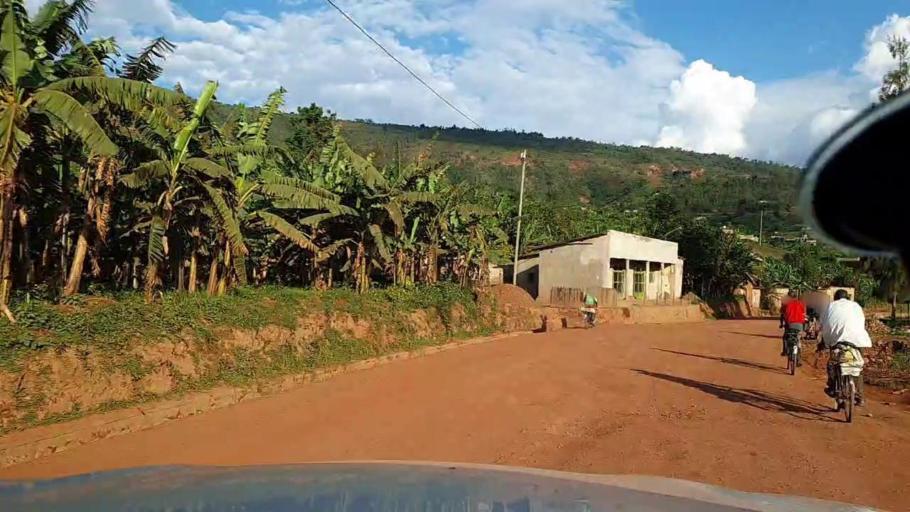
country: RW
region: Kigali
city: Kigali
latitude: -1.9152
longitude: 29.9877
